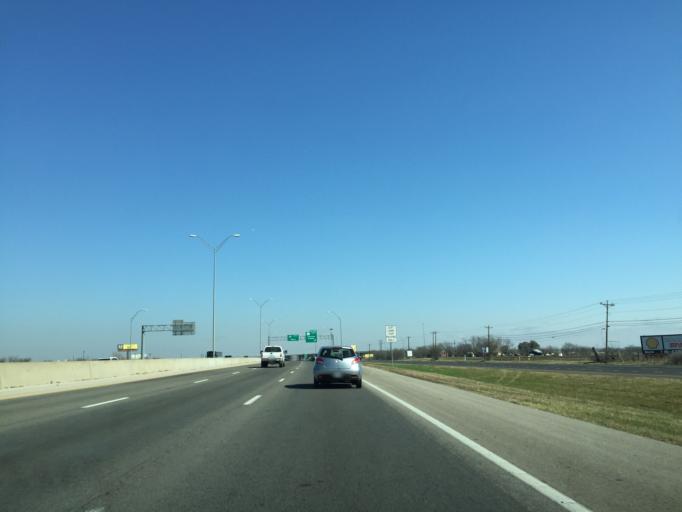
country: US
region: Texas
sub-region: Williamson County
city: Serenada
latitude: 30.6785
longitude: -97.6615
